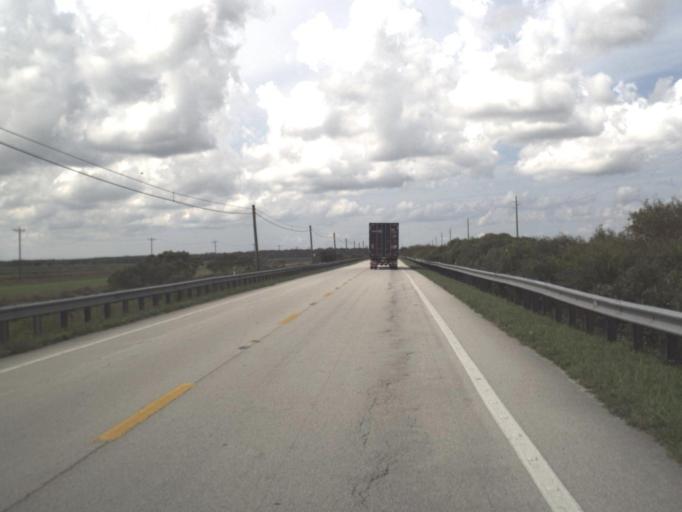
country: US
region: Florida
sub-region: Highlands County
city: Lake Placid
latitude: 27.2087
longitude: -81.2385
